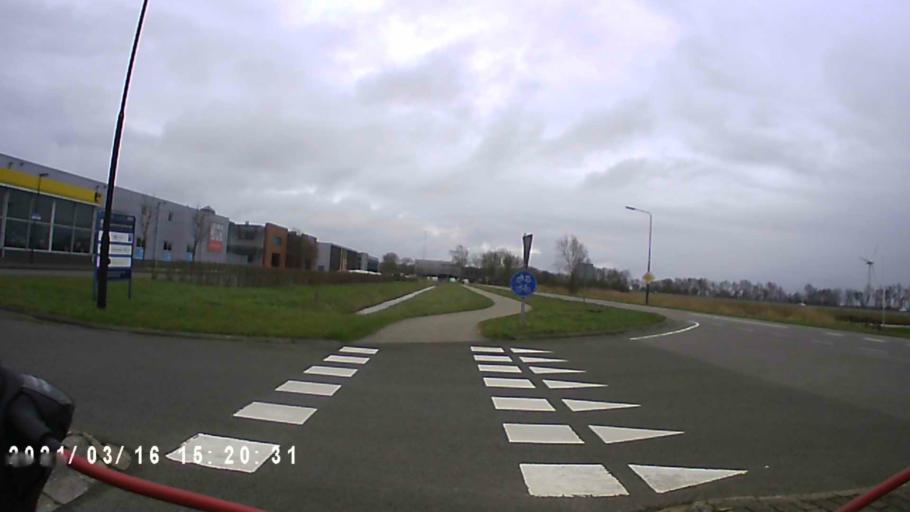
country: NL
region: Friesland
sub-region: Sudwest Fryslan
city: Bolsward
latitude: 53.0651
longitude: 5.5010
